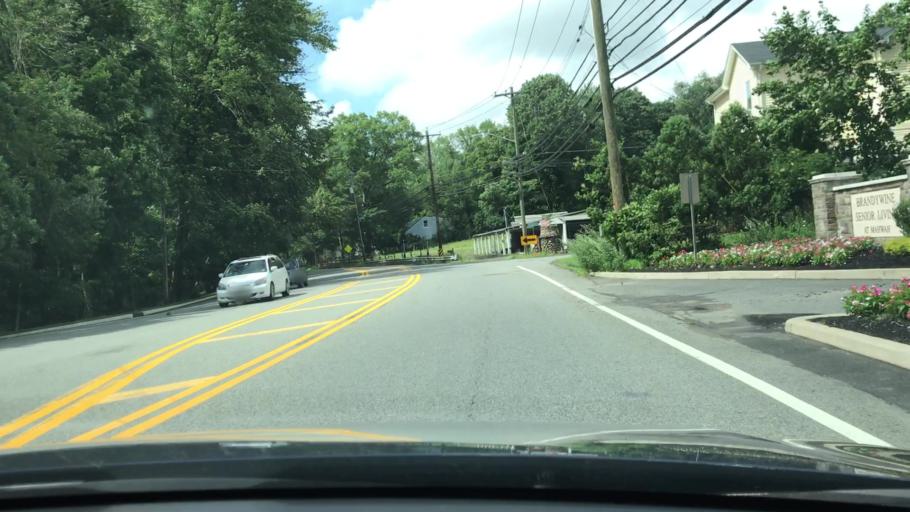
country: US
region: New Jersey
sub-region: Bergen County
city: Wyckoff
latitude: 41.0258
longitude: -74.1679
